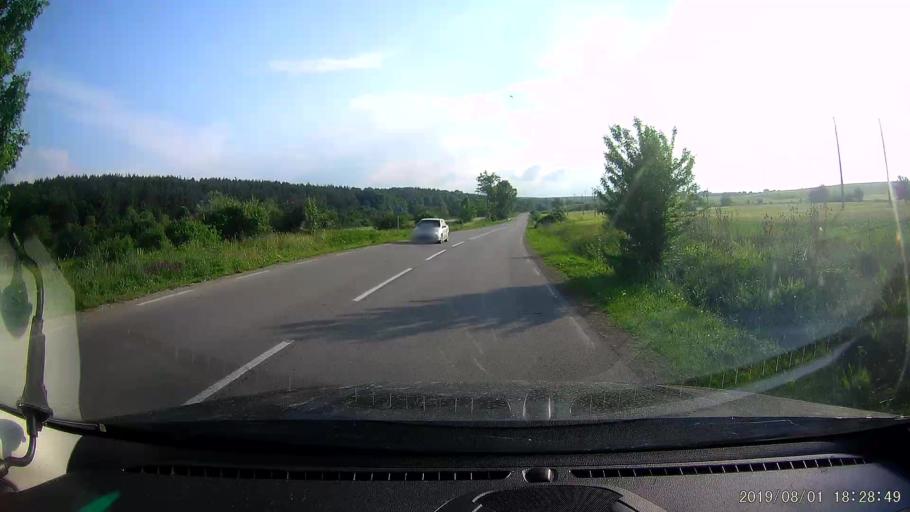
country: BG
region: Shumen
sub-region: Obshtina Venets
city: Venets
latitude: 43.5698
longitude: 26.9560
